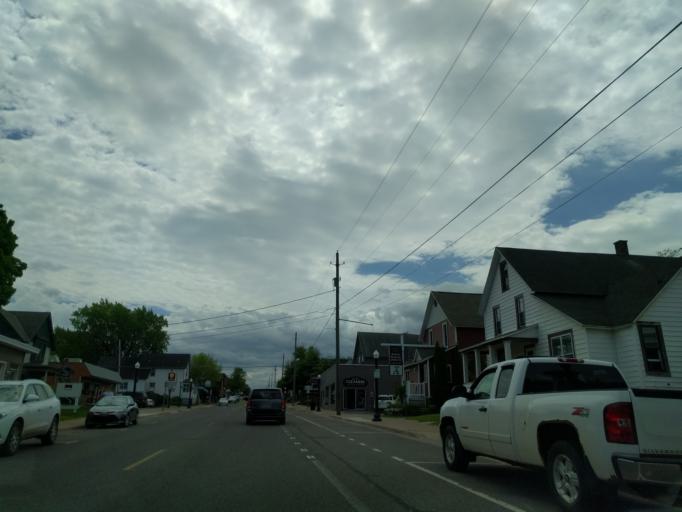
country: US
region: Michigan
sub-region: Marquette County
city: Marquette
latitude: 46.5520
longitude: -87.3948
